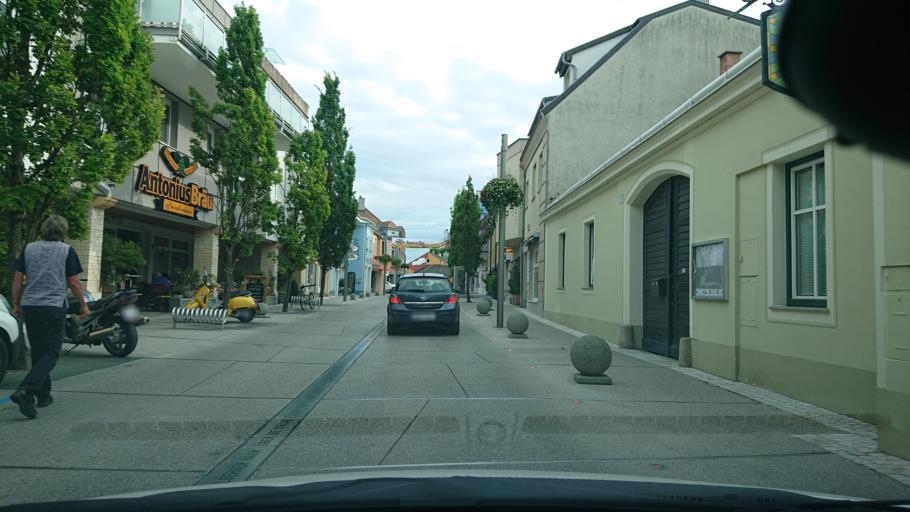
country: AT
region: Lower Austria
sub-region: Politischer Bezirk Baden
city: Leobersdorf
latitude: 47.9279
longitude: 16.2164
